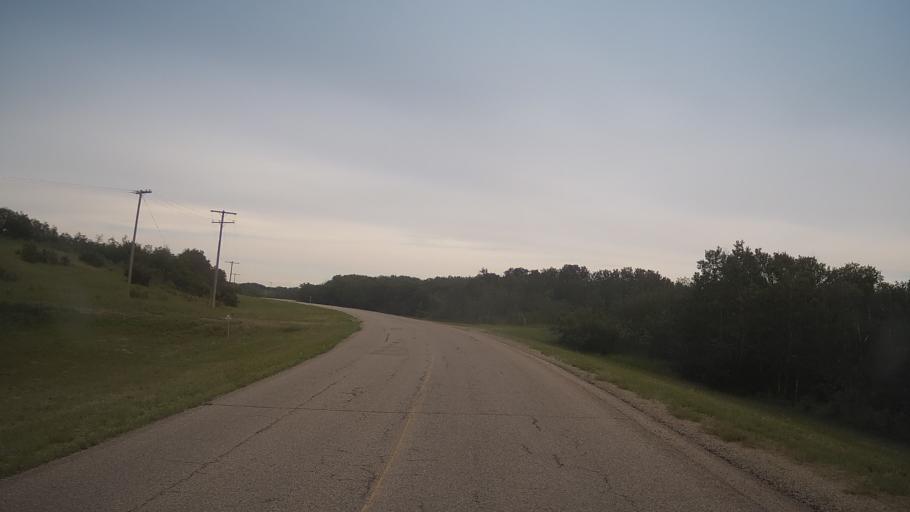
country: CA
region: Saskatchewan
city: Saskatoon
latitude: 51.8468
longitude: -106.5330
